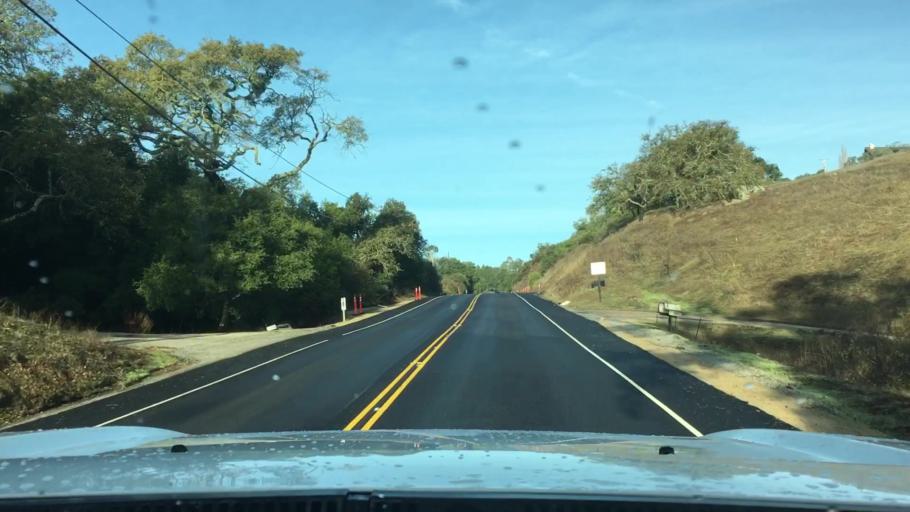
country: US
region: California
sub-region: San Luis Obispo County
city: Atascadero
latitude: 35.4523
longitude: -120.7092
